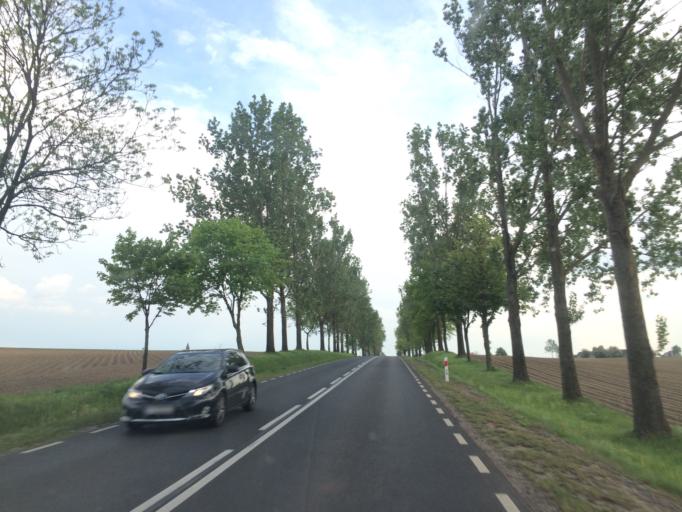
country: PL
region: Kujawsko-Pomorskie
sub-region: Powiat brodnicki
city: Brzozie
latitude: 53.3508
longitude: 19.5684
